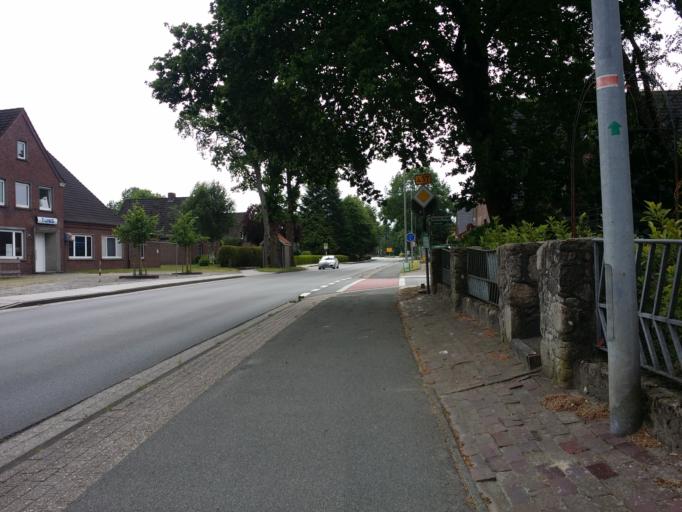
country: DE
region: Lower Saxony
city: Friedeburg
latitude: 53.4348
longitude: 7.8565
